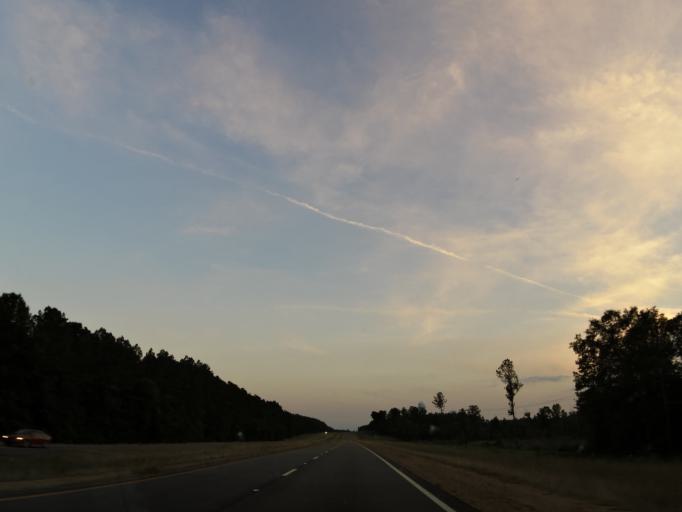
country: US
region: Mississippi
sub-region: Kemper County
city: De Kalb
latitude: 32.7564
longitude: -88.4660
